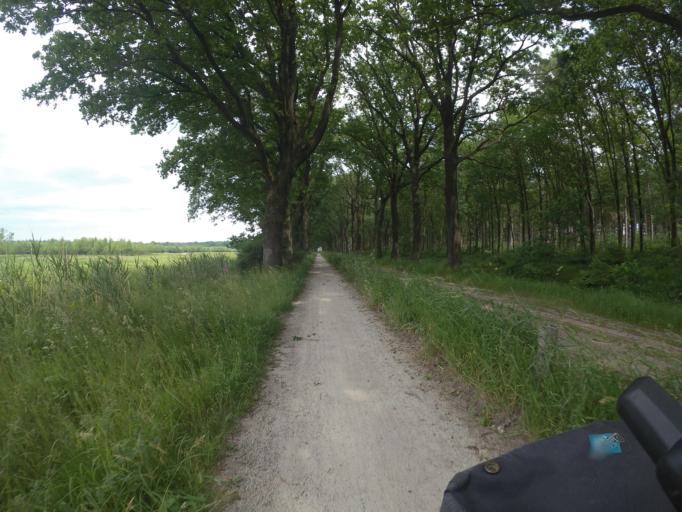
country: NL
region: Drenthe
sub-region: Gemeente Assen
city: Assen
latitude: 53.0089
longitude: 6.4404
